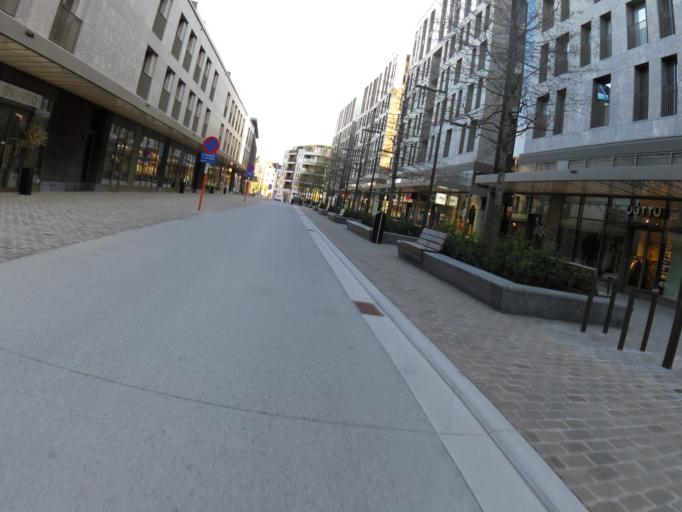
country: BE
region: Flanders
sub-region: Provincie Limburg
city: Hasselt
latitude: 50.9360
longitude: 5.3360
